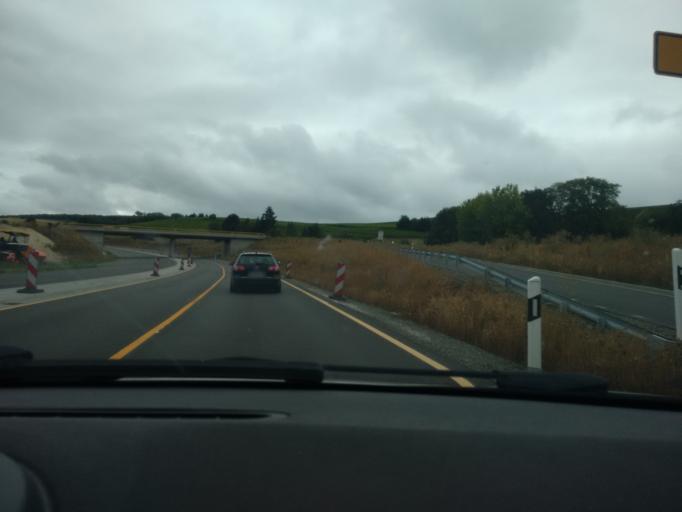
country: DE
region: Rheinland-Pfalz
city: Waldbockelheim
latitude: 49.8202
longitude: 7.7215
